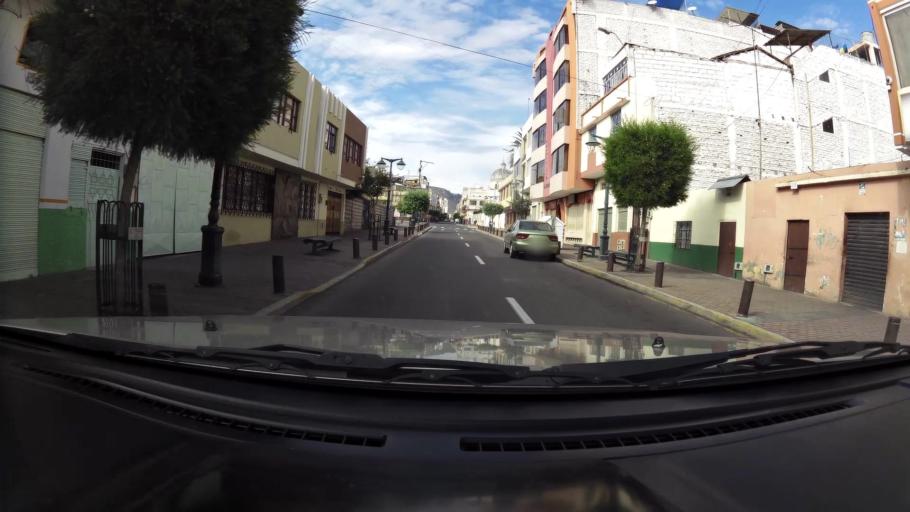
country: EC
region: Tungurahua
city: Ambato
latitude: -1.2346
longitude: -78.6272
